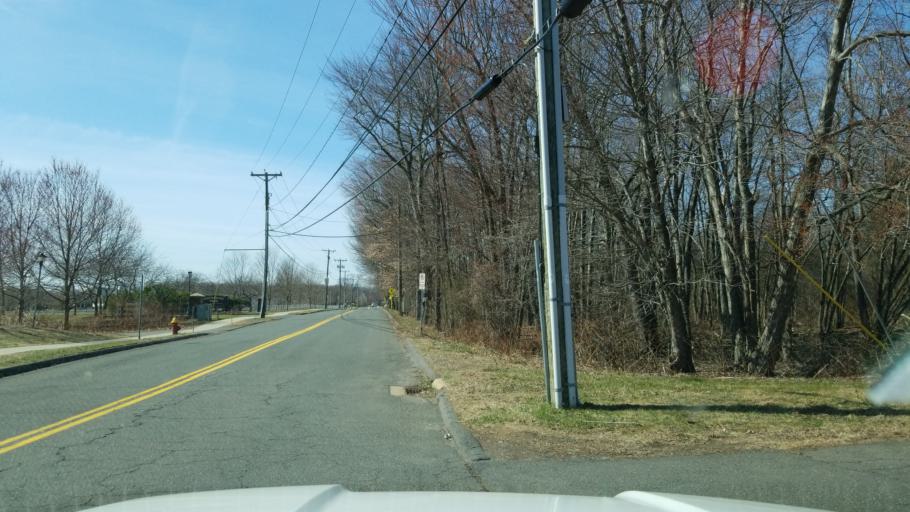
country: US
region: Connecticut
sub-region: Hartford County
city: Glastonbury
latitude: 41.7134
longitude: -72.6114
